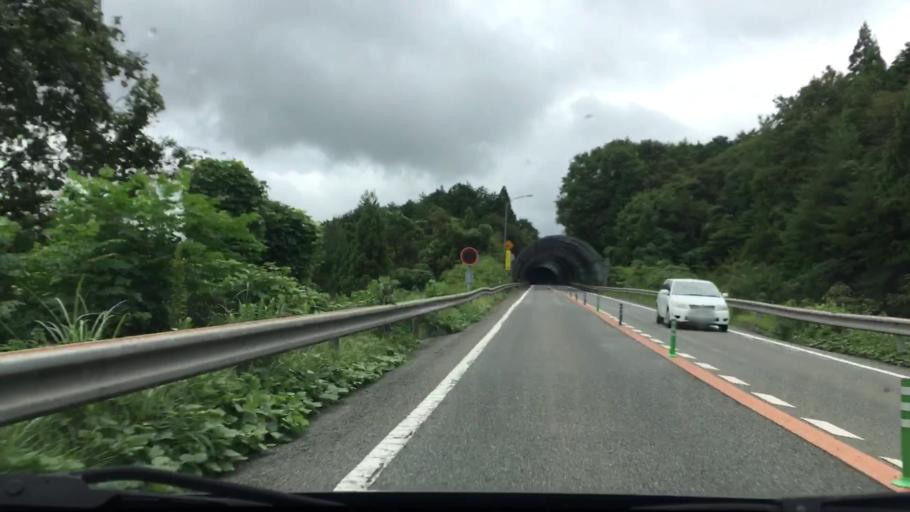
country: JP
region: Hyogo
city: Nishiwaki
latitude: 35.0808
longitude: 134.7732
